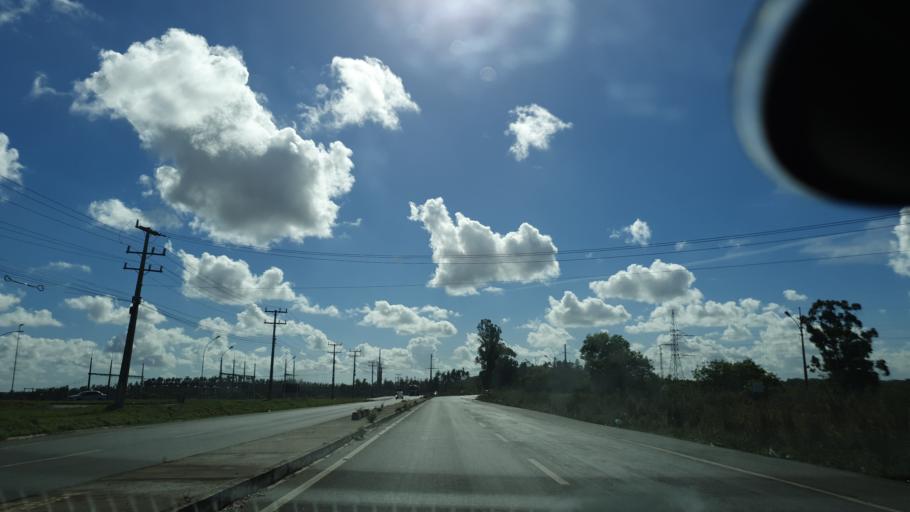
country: BR
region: Bahia
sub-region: Camacari
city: Camacari
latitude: -12.6842
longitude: -38.2688
